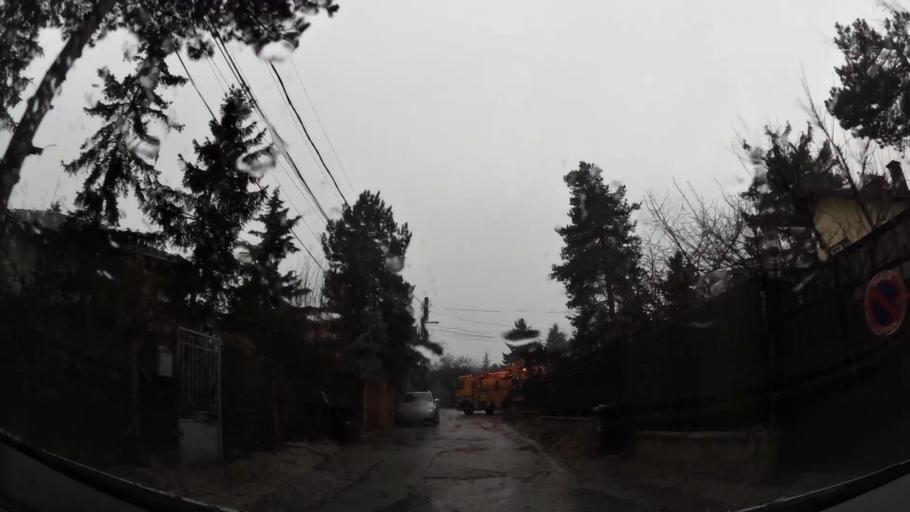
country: BG
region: Sofia-Capital
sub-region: Stolichna Obshtina
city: Sofia
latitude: 42.6283
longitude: 23.3659
